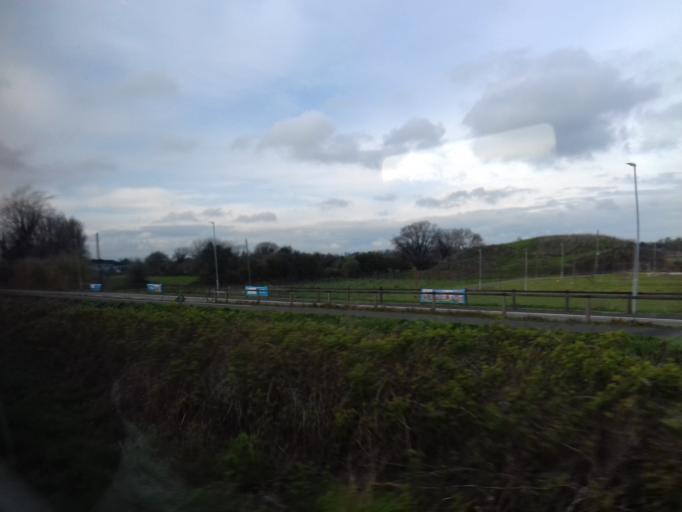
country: IE
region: Leinster
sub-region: Kildare
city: Kilcock
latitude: 53.3963
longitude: -6.6599
